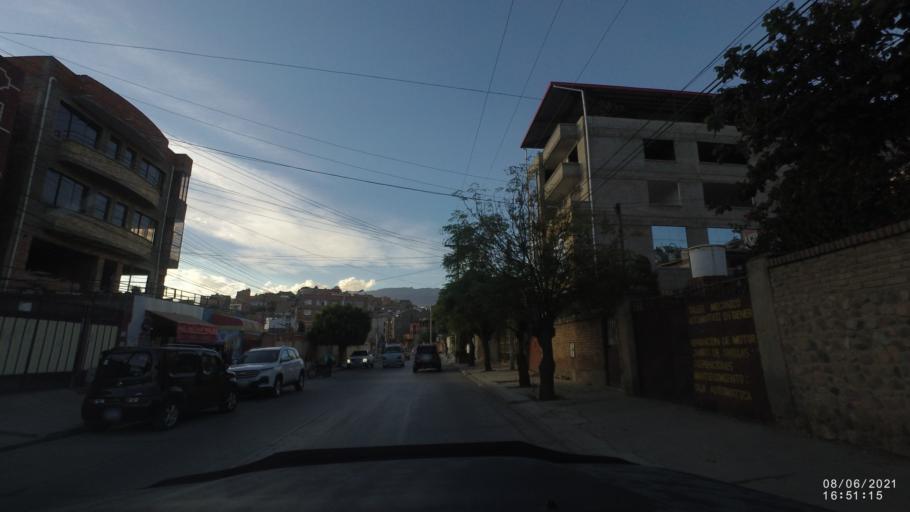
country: BO
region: Cochabamba
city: Cochabamba
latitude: -17.4102
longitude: -66.1463
